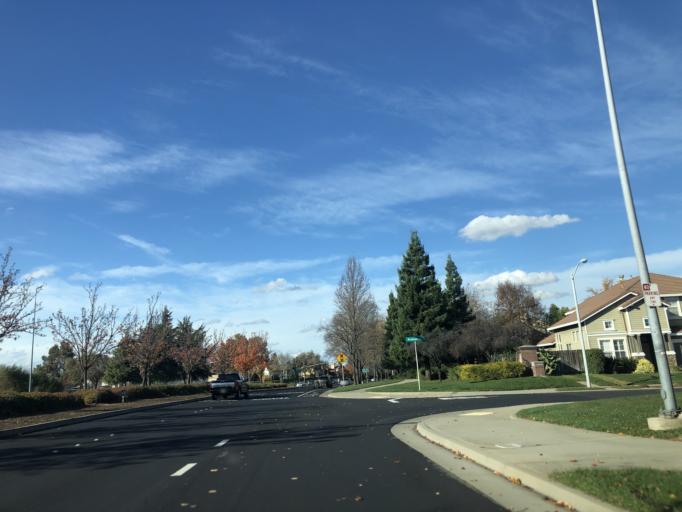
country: US
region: California
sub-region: Placer County
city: Roseville
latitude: 38.7808
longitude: -121.2922
